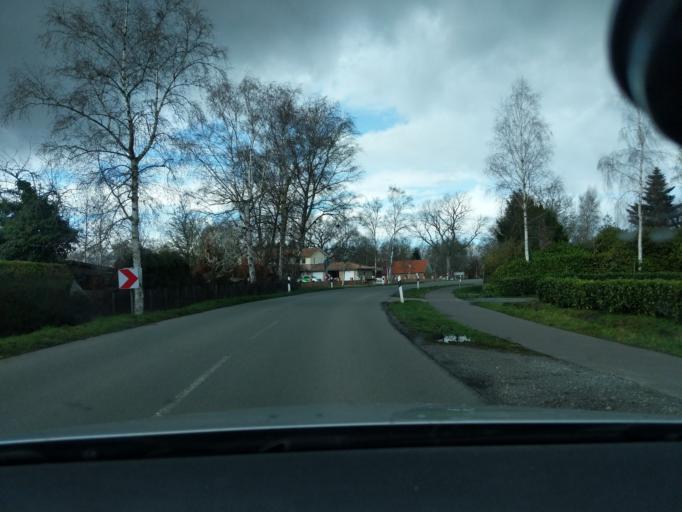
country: DE
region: Lower Saxony
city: Drochtersen
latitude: 53.6538
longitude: 9.4260
